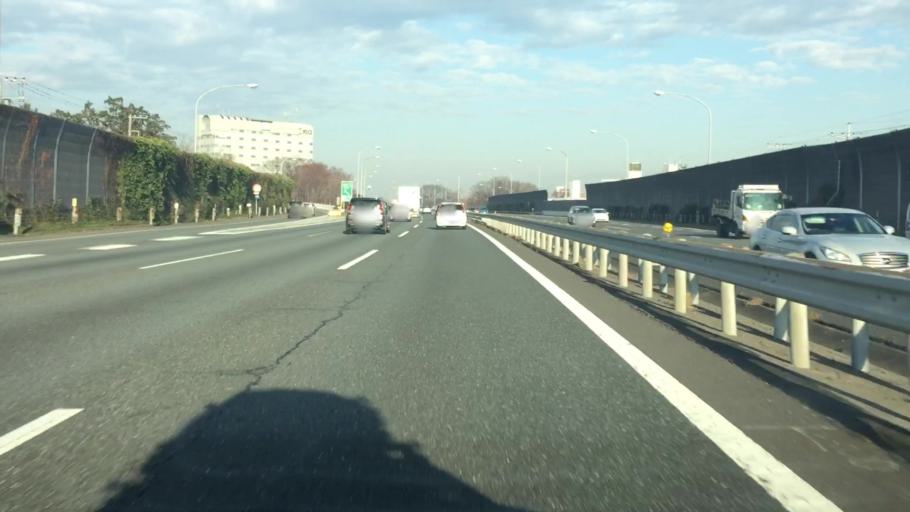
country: JP
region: Saitama
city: Sakado
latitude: 35.9436
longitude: 139.4009
